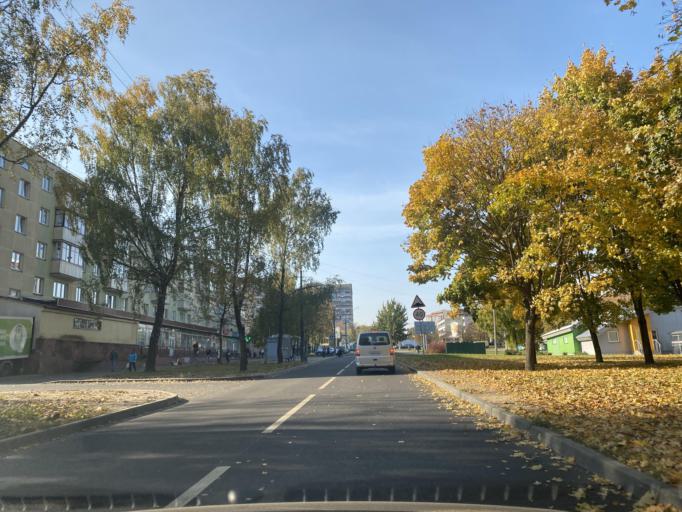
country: BY
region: Minsk
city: Borovlyany
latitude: 53.9534
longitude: 27.6227
